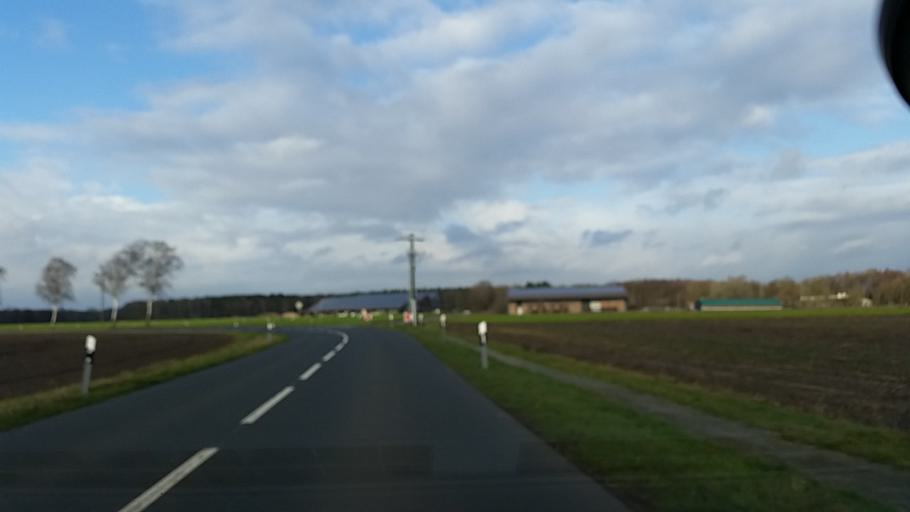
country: DE
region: Lower Saxony
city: Wrestedt
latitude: 52.9048
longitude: 10.5654
